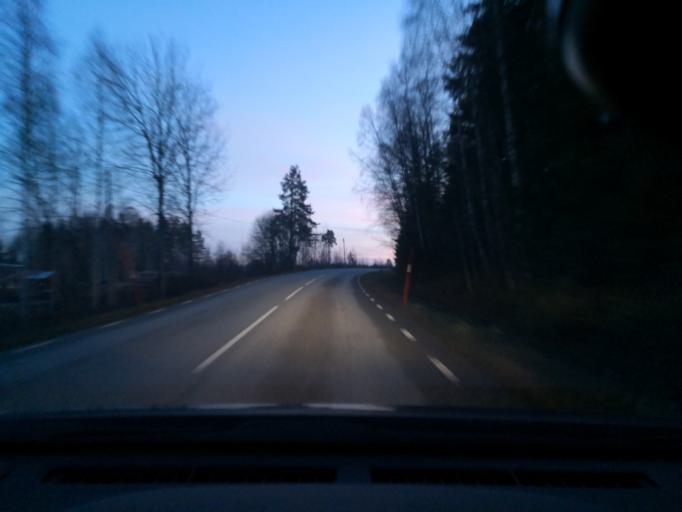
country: SE
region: OErebro
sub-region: Lindesbergs Kommun
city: Frovi
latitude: 59.3678
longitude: 15.4311
